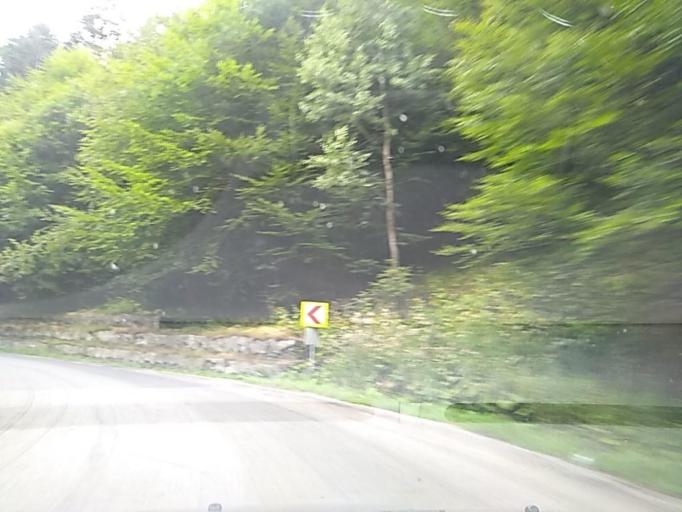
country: RO
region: Brasov
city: Crivina
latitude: 45.4734
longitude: 25.9333
